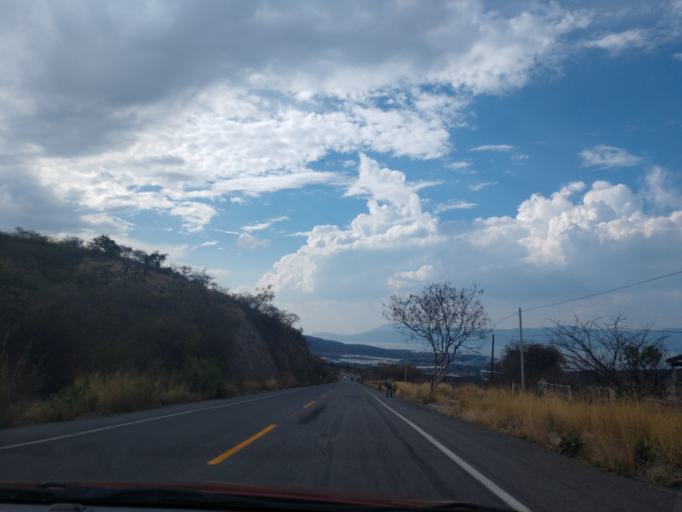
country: MX
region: Jalisco
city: La Manzanilla de la Paz
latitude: 20.1260
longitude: -103.1599
